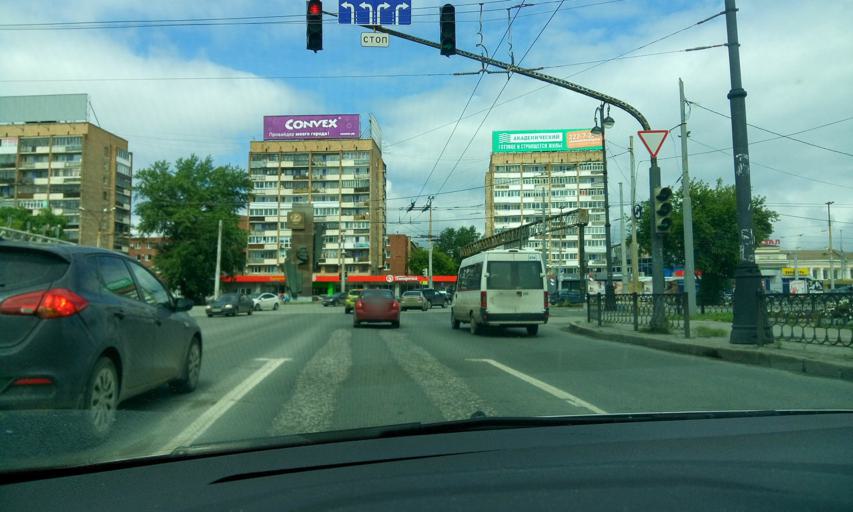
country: RU
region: Sverdlovsk
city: Yekaterinburg
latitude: 56.8558
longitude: 60.6042
